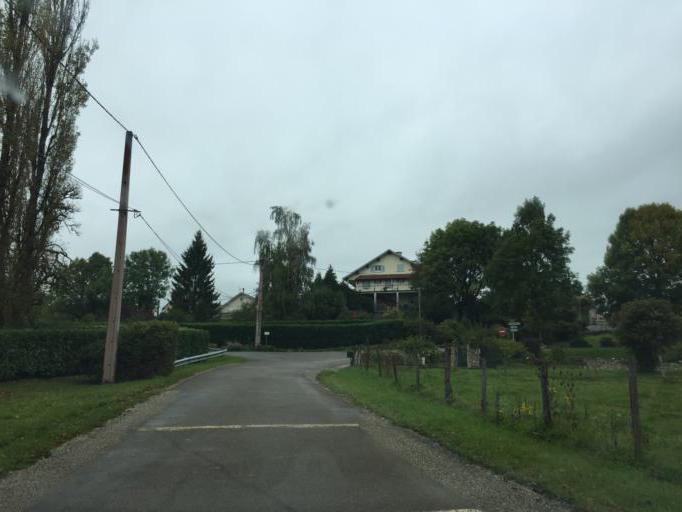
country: FR
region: Franche-Comte
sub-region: Departement du Jura
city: Orgelet
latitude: 46.5311
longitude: 5.6328
